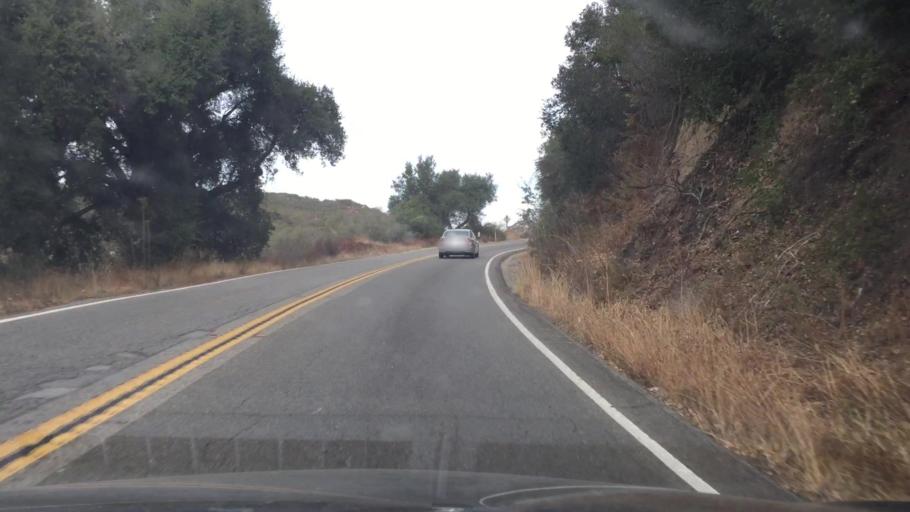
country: US
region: California
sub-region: Riverside County
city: Lakeland Village
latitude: 33.6081
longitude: -117.4308
